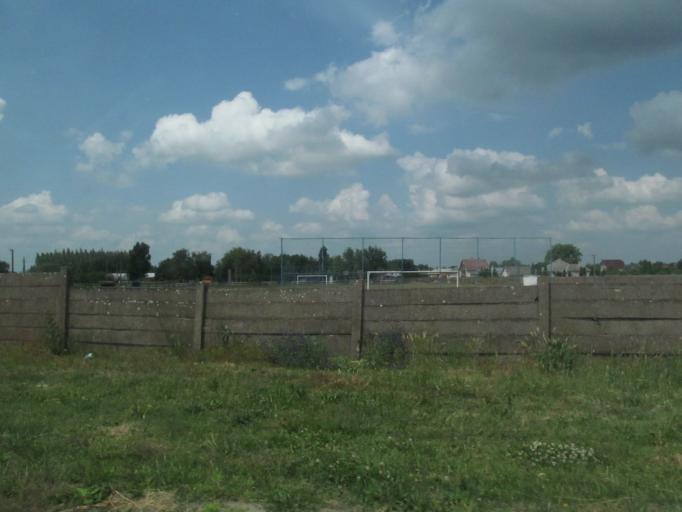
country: HU
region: Szabolcs-Szatmar-Bereg
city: Nagykallo
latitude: 47.8730
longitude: 21.8565
